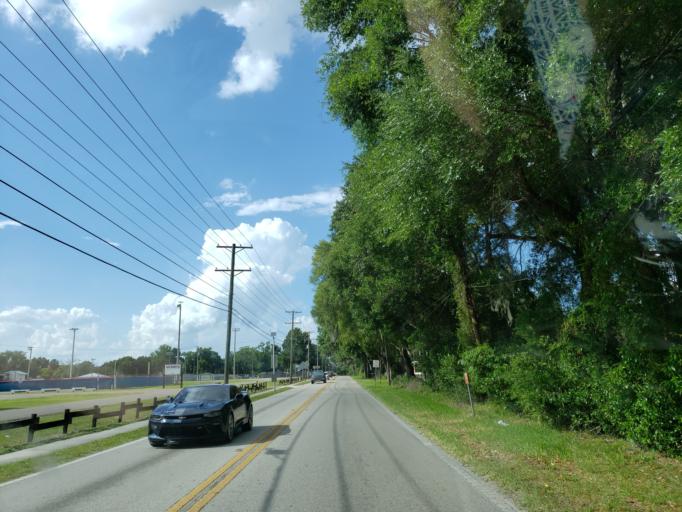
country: US
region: Florida
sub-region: Hillsborough County
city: Seffner
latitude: 27.9671
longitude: -82.2777
